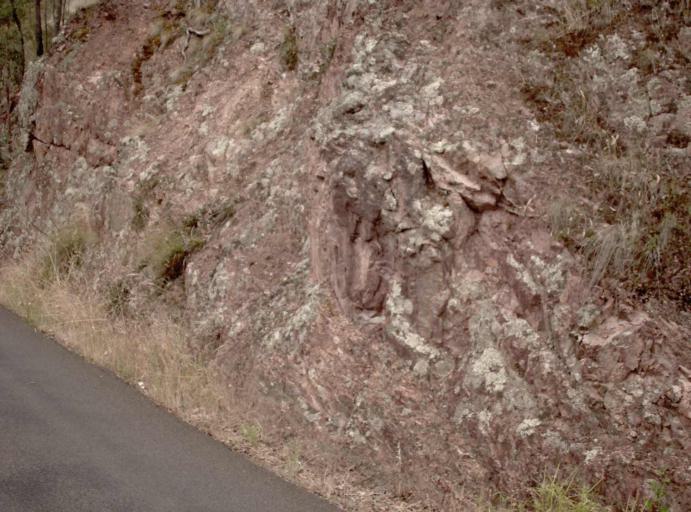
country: AU
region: Victoria
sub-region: Wellington
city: Heyfield
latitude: -37.7014
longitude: 146.6613
